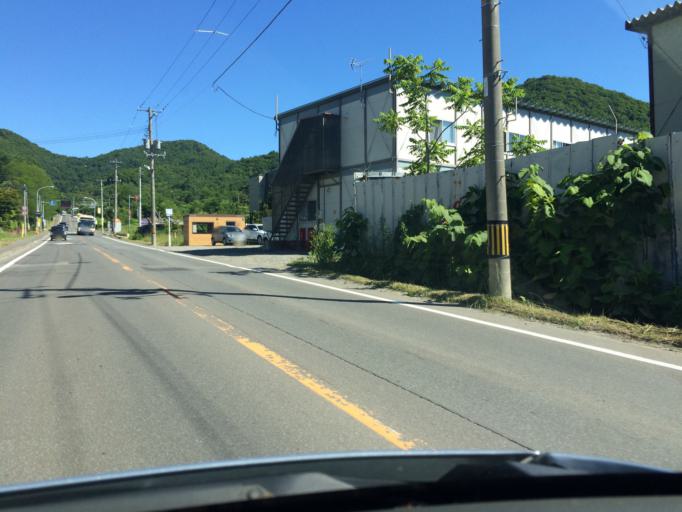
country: JP
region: Hokkaido
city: Sapporo
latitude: 43.0125
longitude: 141.3036
